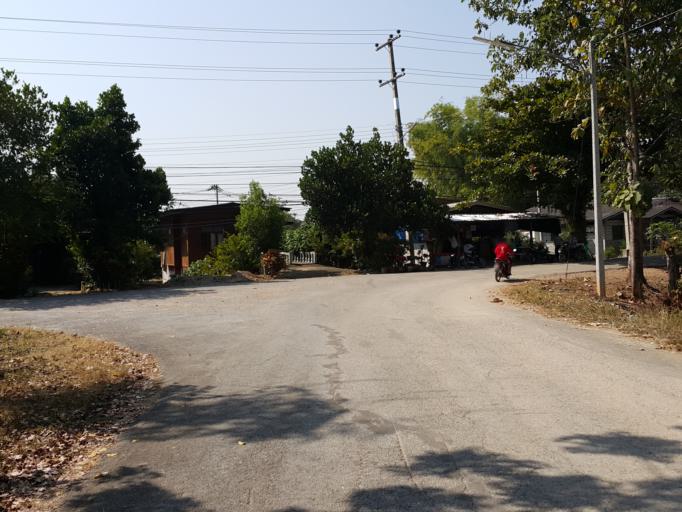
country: TH
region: Lamphun
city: Pa Sang
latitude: 18.5424
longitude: 98.9412
